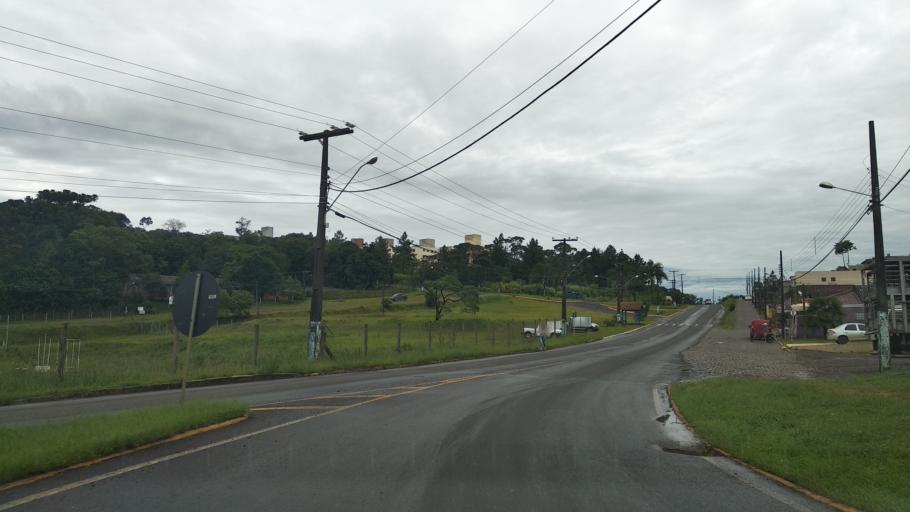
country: BR
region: Santa Catarina
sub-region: Videira
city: Videira
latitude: -26.9918
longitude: -51.1815
